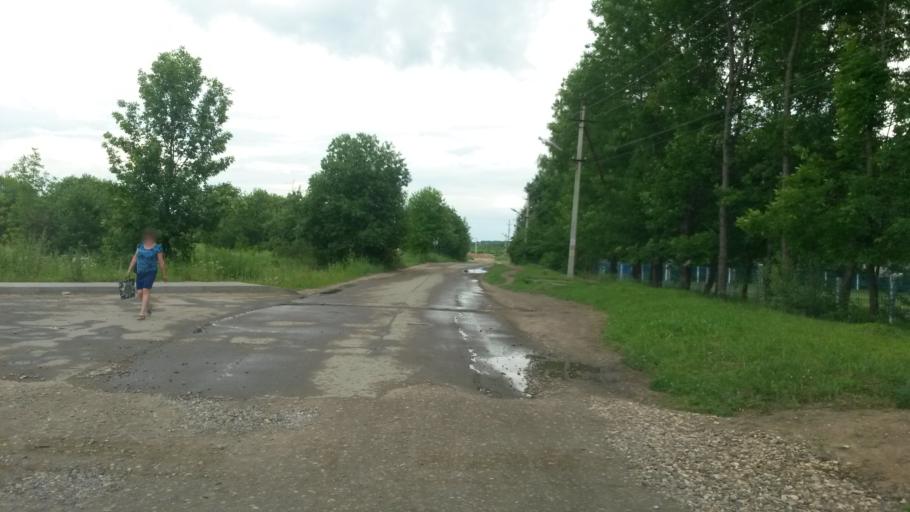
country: RU
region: Jaroslavl
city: Gavrilov-Yam
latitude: 57.3025
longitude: 39.8699
